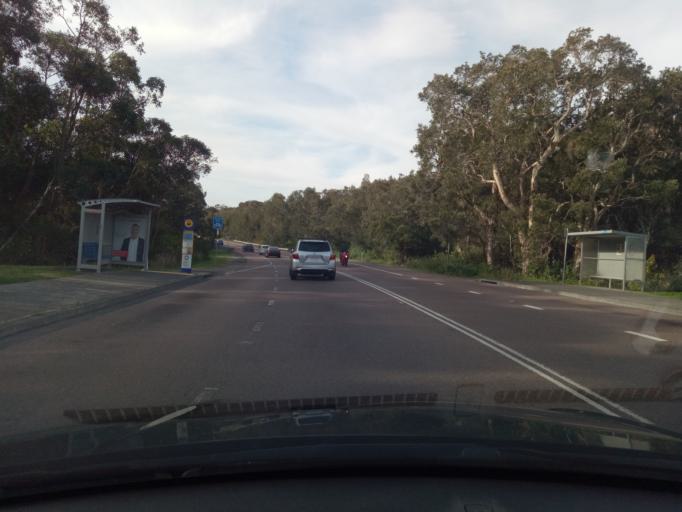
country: AU
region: New South Wales
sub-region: Gosford Shire
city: Forresters Beach
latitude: -33.3963
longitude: 151.4736
